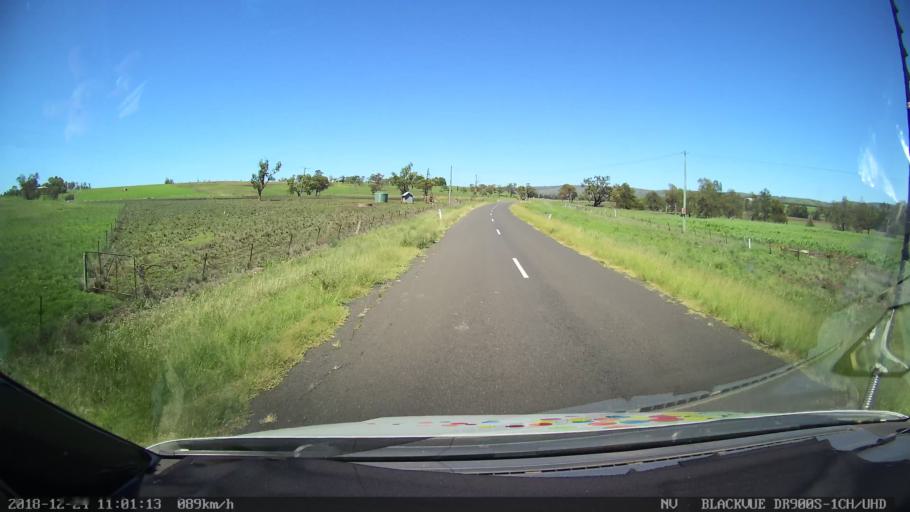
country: AU
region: New South Wales
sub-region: Upper Hunter Shire
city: Merriwa
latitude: -32.0747
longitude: 150.3867
